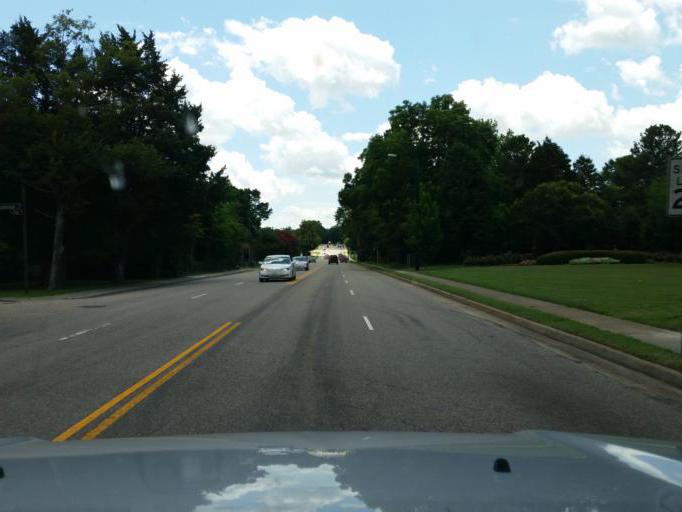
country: US
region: Virginia
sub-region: City of Williamsburg
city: Williamsburg
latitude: 37.2773
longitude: -76.6900
